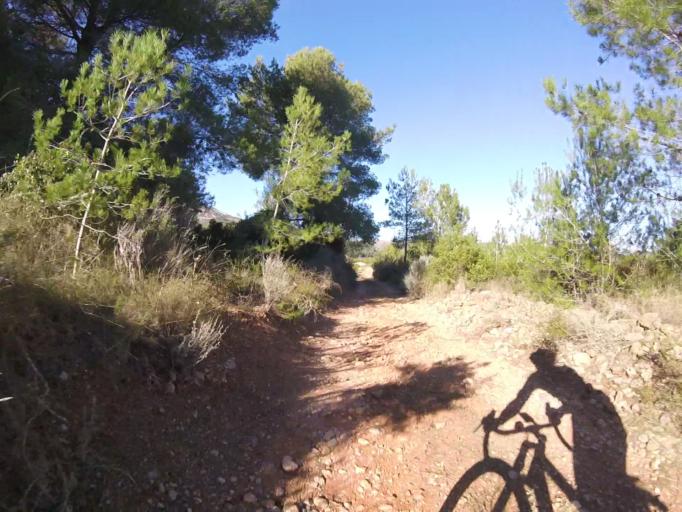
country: ES
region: Valencia
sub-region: Provincia de Castello
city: Orpesa/Oropesa del Mar
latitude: 40.1214
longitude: 0.1149
